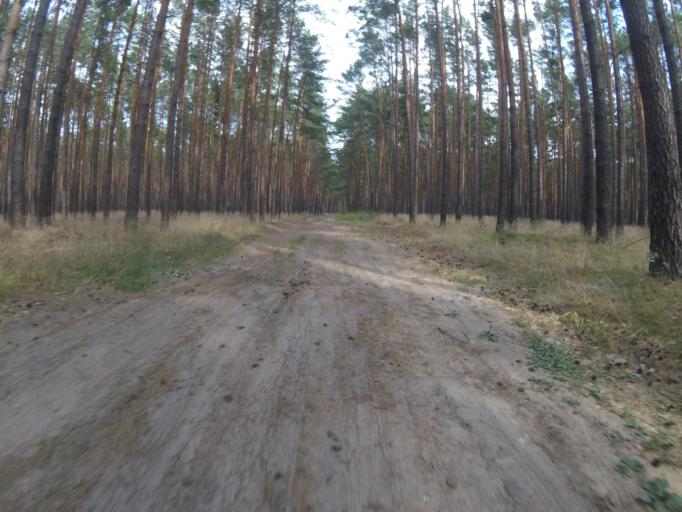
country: DE
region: Brandenburg
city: Wildau
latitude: 52.3181
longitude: 13.7301
